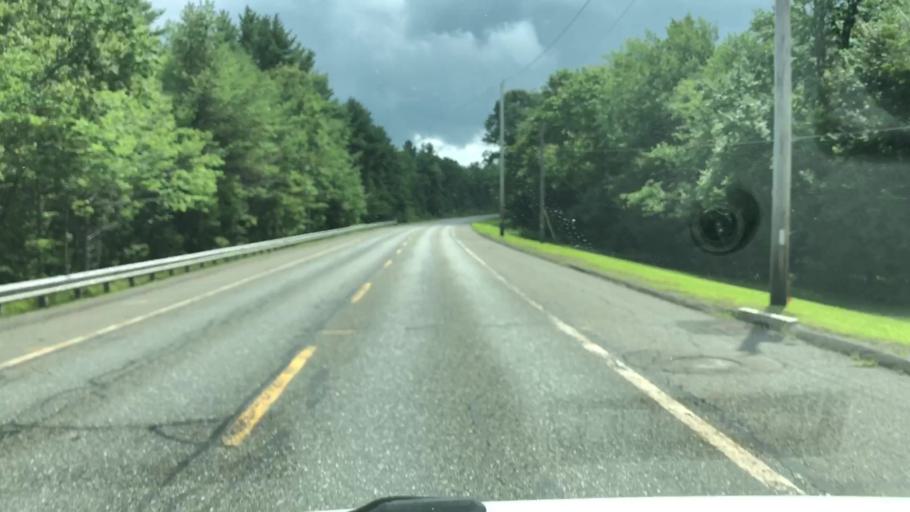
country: US
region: Massachusetts
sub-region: Franklin County
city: Ashfield
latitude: 42.4664
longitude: -72.8075
